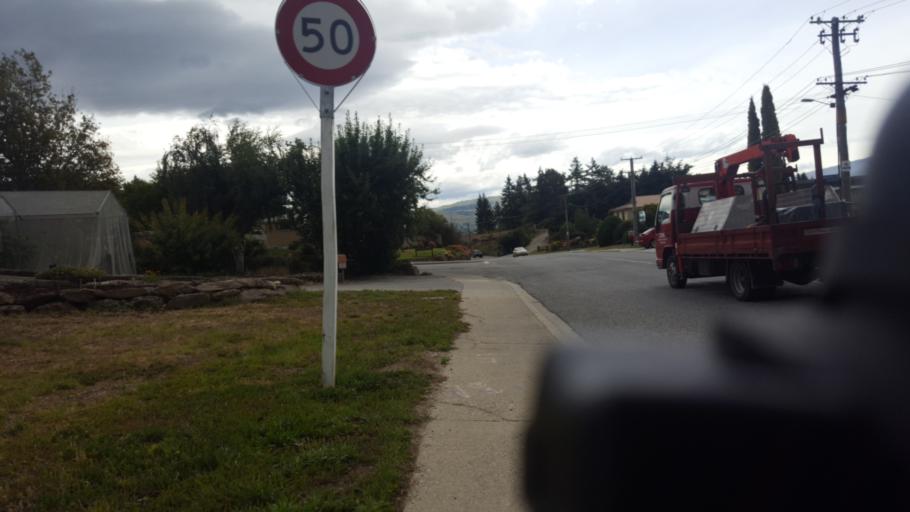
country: NZ
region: Otago
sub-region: Queenstown-Lakes District
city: Wanaka
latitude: -45.2609
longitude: 169.3878
